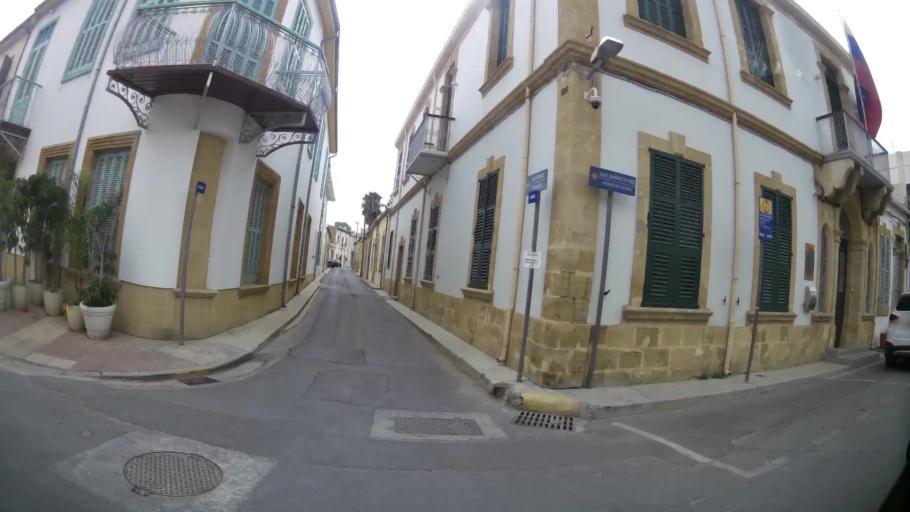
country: CY
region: Lefkosia
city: Nicosia
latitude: 35.1725
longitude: 33.3685
